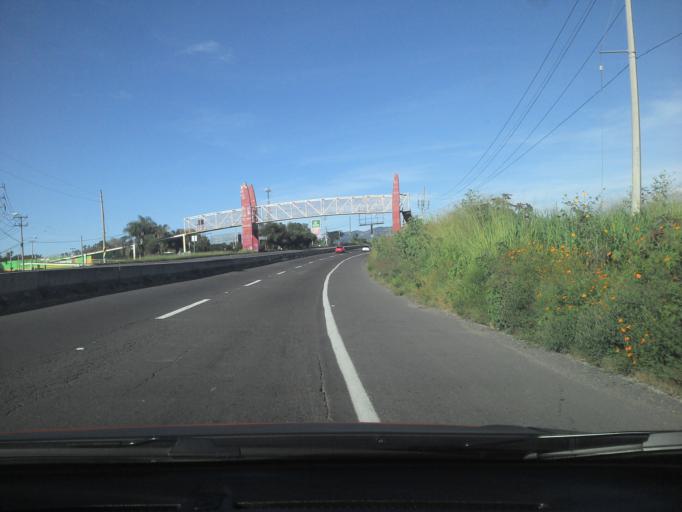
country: MX
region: Jalisco
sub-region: Tala
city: Los Ruisenores
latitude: 20.7020
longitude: -103.6881
